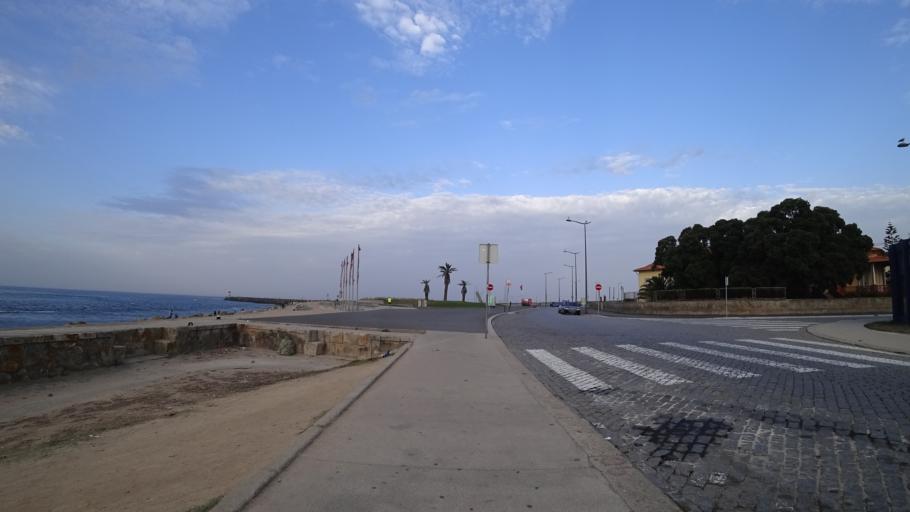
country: PT
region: Porto
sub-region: Vila Nova de Gaia
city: Canidelo
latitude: 41.1476
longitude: -8.6728
